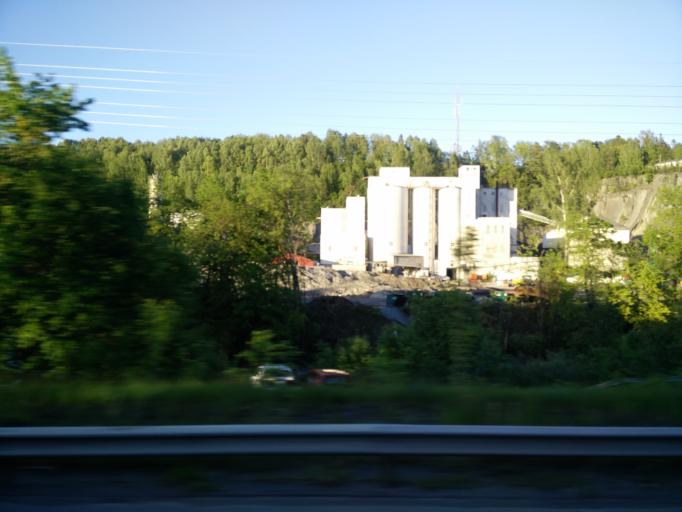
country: NO
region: Akershus
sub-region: Asker
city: Billingstad
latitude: 59.9000
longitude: 10.4958
